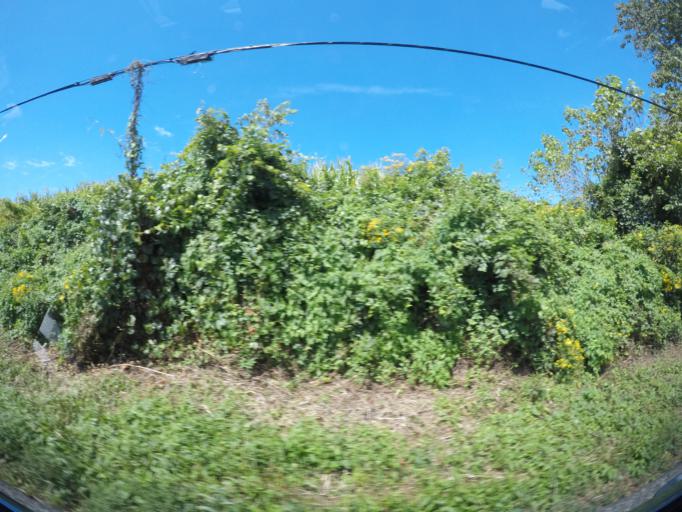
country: US
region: Maryland
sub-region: Harford County
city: South Bel Air
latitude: 39.5889
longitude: -76.2937
